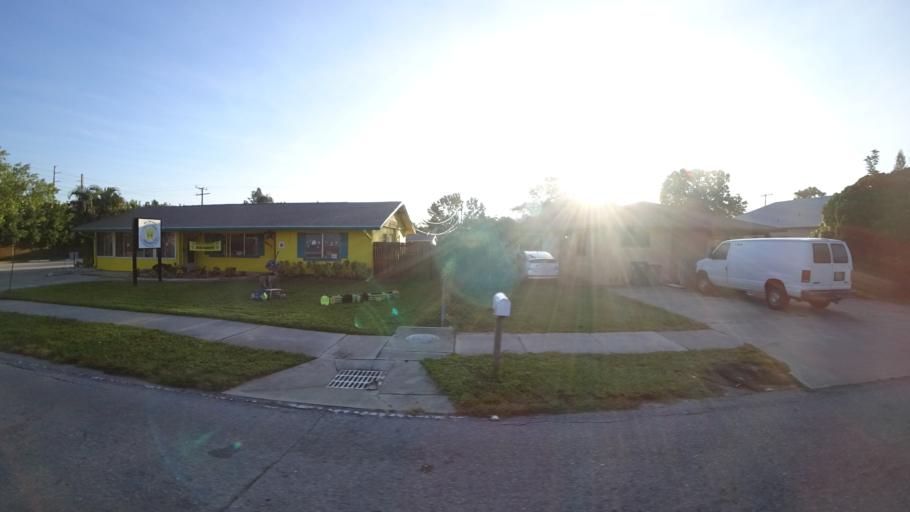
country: US
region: Florida
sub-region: Manatee County
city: South Bradenton
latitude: 27.4613
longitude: -82.5819
